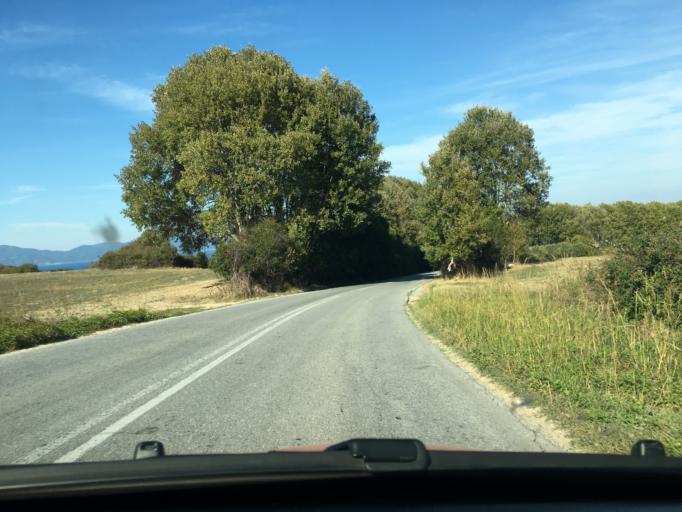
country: GR
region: Central Macedonia
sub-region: Nomos Chalkidikis
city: Ierissos
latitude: 40.3873
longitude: 23.8921
